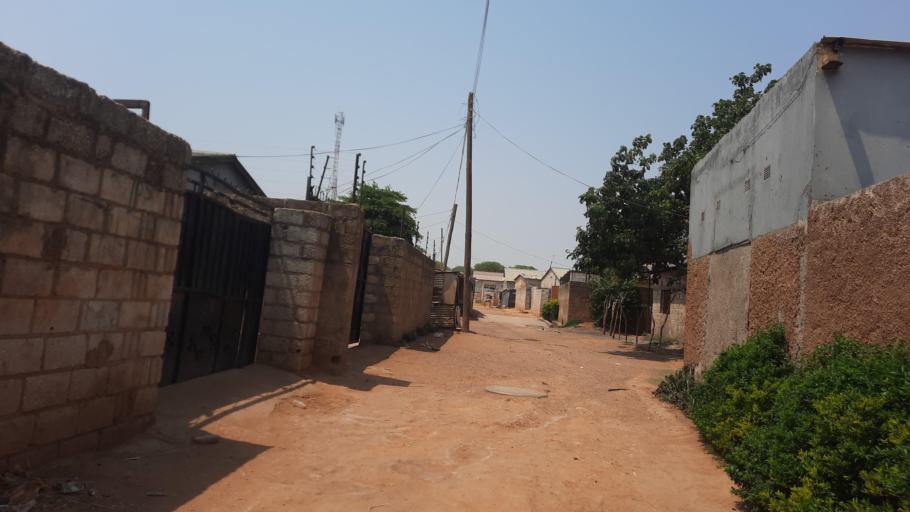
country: ZM
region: Lusaka
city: Lusaka
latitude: -15.3935
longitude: 28.3789
